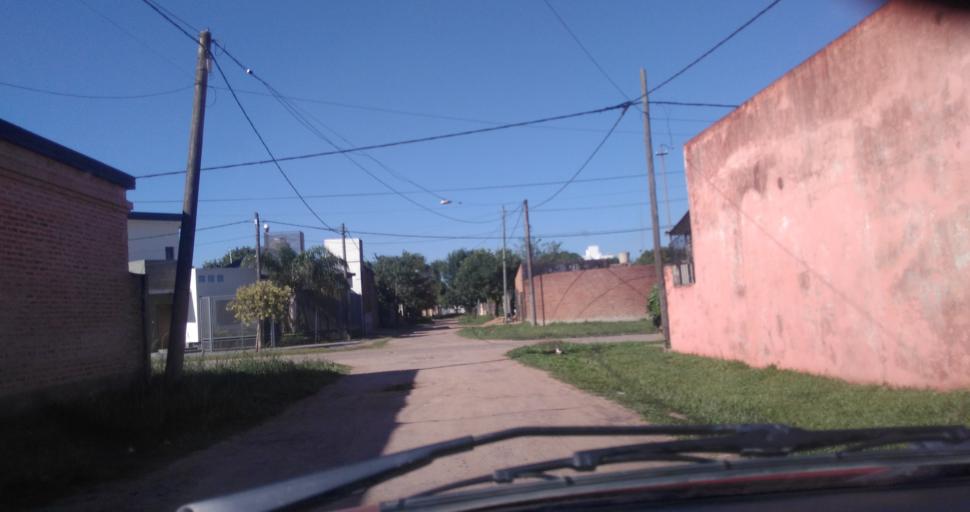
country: AR
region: Chaco
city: Resistencia
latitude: -27.4482
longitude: -58.9681
